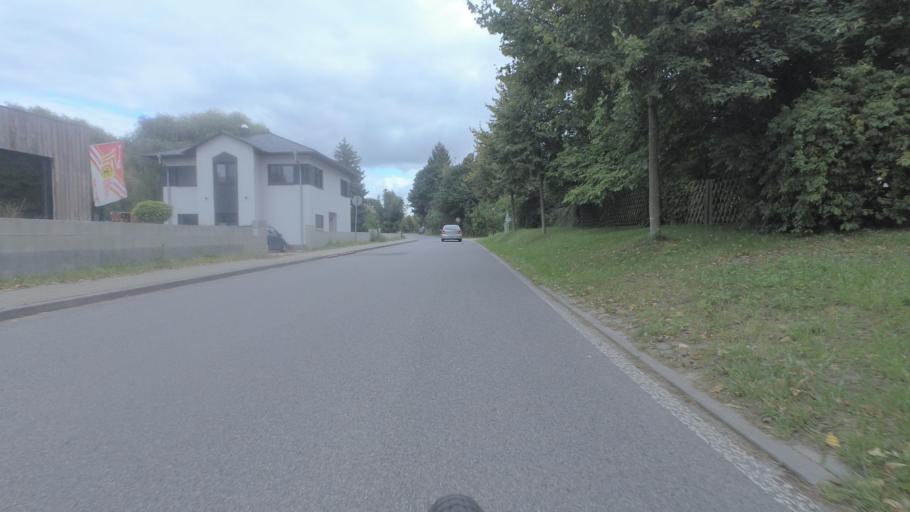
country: DE
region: Brandenburg
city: Melchow
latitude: 52.7728
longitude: 13.7041
